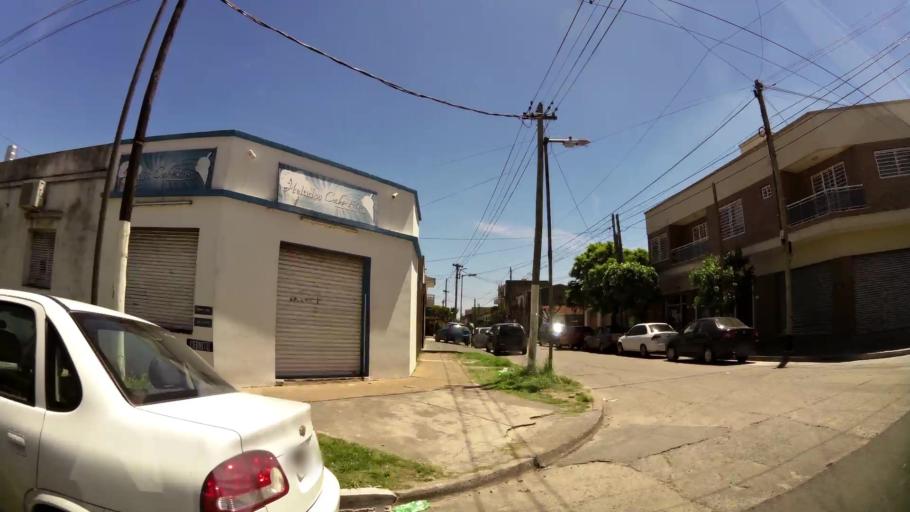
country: AR
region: Buenos Aires
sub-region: Partido de Quilmes
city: Quilmes
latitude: -34.7220
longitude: -58.3059
